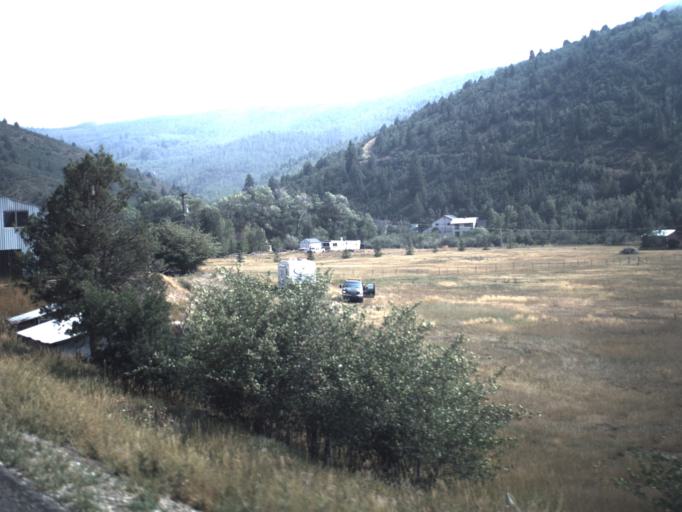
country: US
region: Utah
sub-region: Summit County
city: Francis
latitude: 40.6186
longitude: -111.2155
